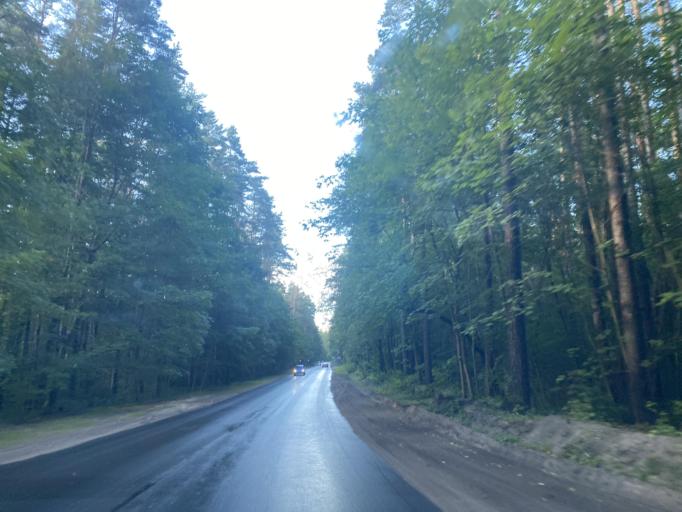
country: BY
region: Minsk
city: Borovlyany
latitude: 53.9191
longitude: 27.6541
